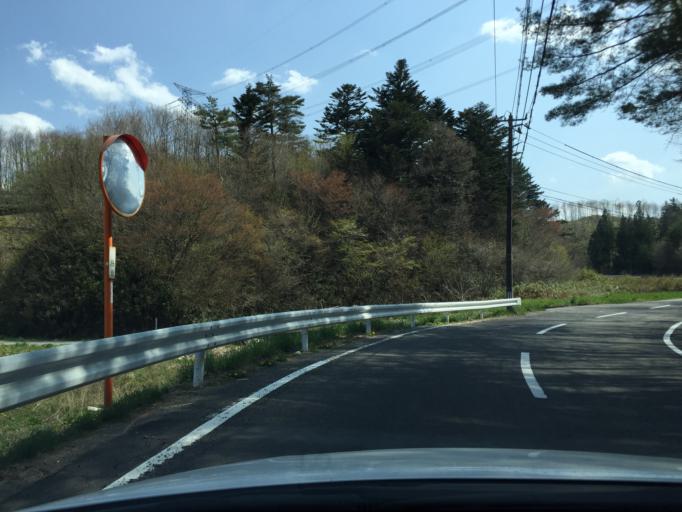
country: JP
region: Fukushima
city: Namie
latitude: 37.3868
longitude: 140.7989
